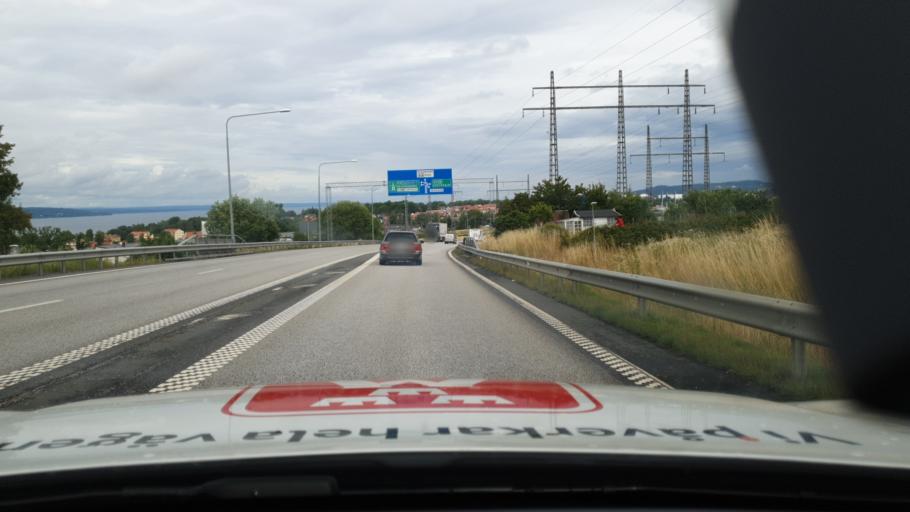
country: SE
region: Joenkoeping
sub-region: Jonkopings Kommun
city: Jonkoping
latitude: 57.7741
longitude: 14.2195
